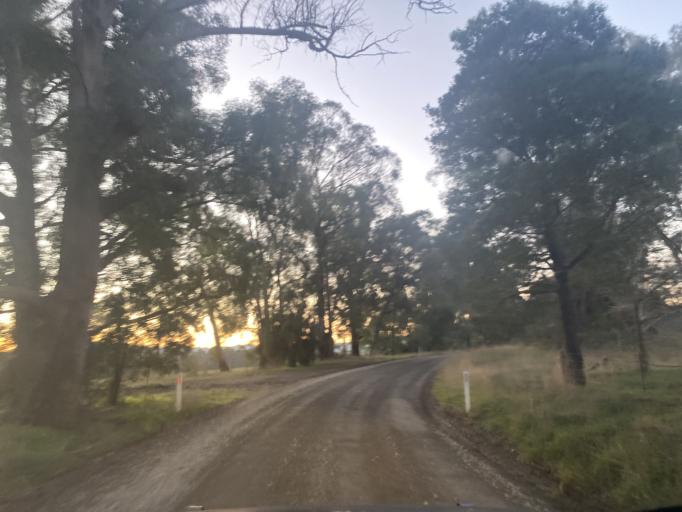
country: AU
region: Victoria
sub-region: Murrindindi
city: Kinglake West
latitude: -37.4108
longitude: 145.4625
